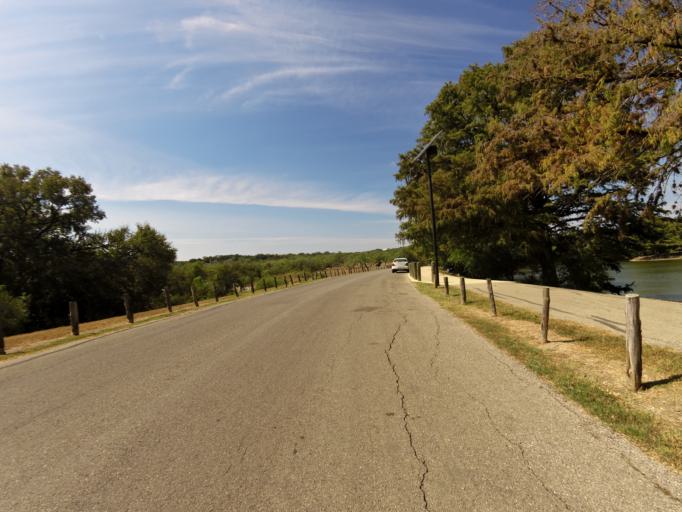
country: US
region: Texas
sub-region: Bexar County
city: San Antonio
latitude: 29.3849
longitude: -98.4269
